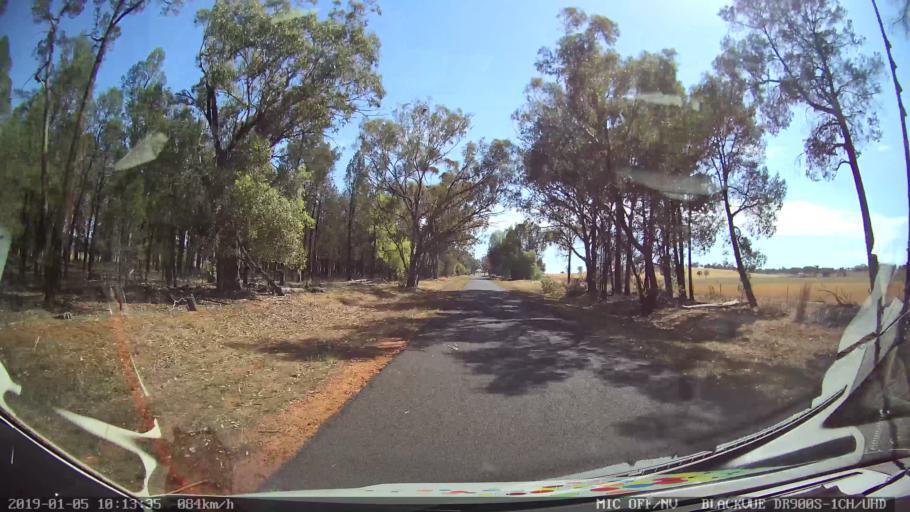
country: AU
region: New South Wales
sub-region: Gilgandra
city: Gilgandra
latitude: -31.6009
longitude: 148.9263
